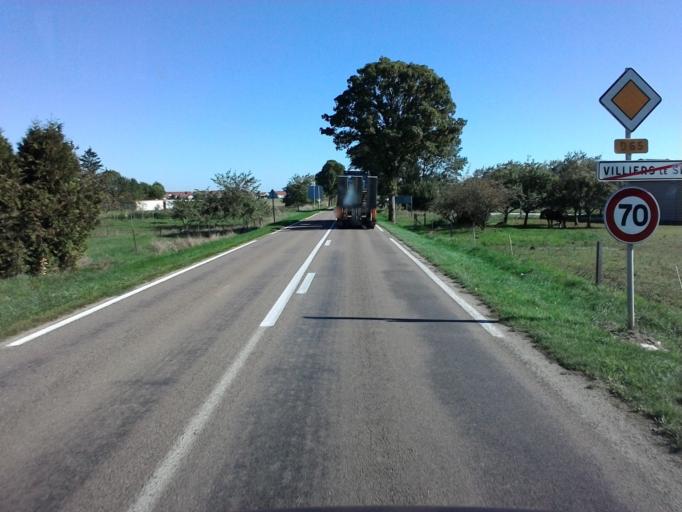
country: FR
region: Champagne-Ardenne
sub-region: Departement de la Haute-Marne
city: Chaumont
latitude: 48.1014
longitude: 5.0616
